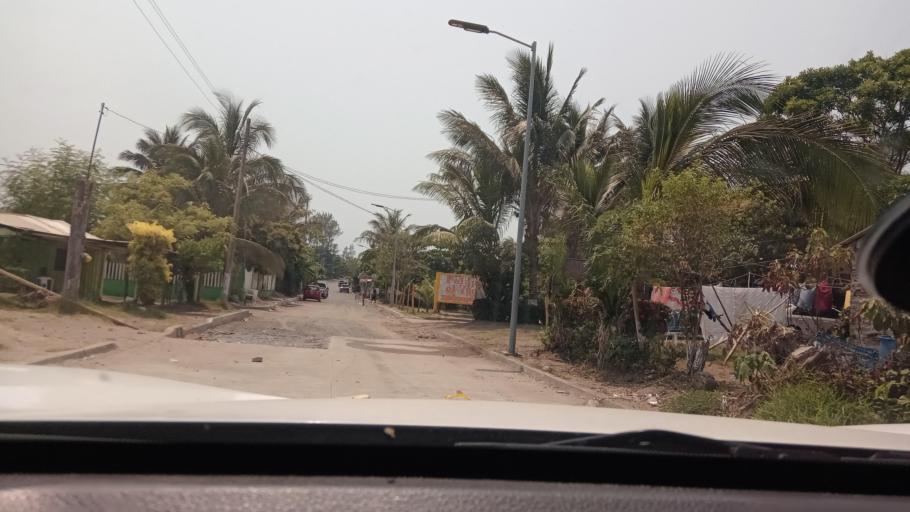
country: MX
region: Veracruz
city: Catemaco
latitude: 18.5558
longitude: -94.9896
